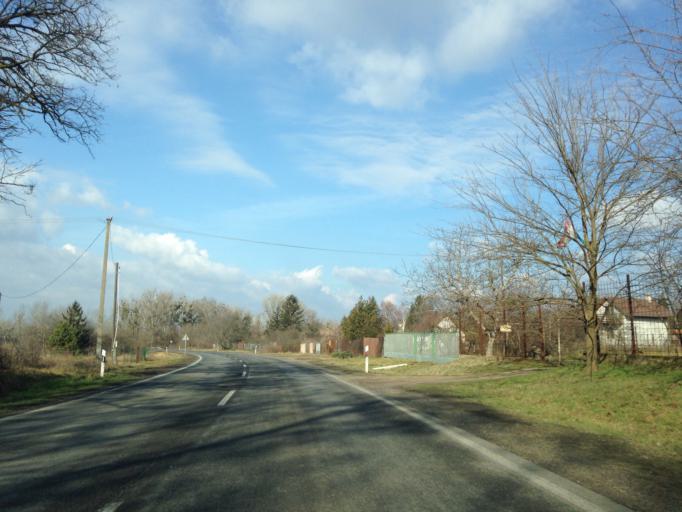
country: HU
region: Komarom-Esztergom
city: Szomod
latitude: 47.6955
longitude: 18.3074
